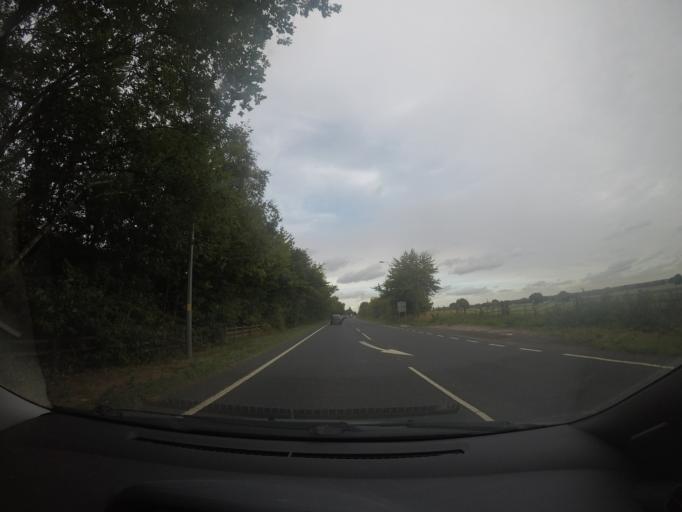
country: GB
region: England
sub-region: North Yorkshire
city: Riccall
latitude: 53.8324
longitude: -1.0534
